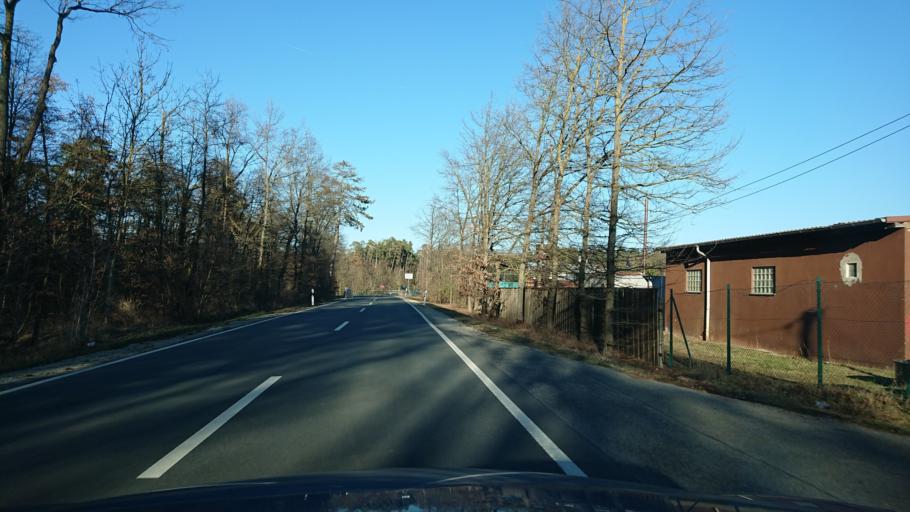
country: DE
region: Bavaria
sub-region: Upper Franconia
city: Pinzberg
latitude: 49.6910
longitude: 11.0835
